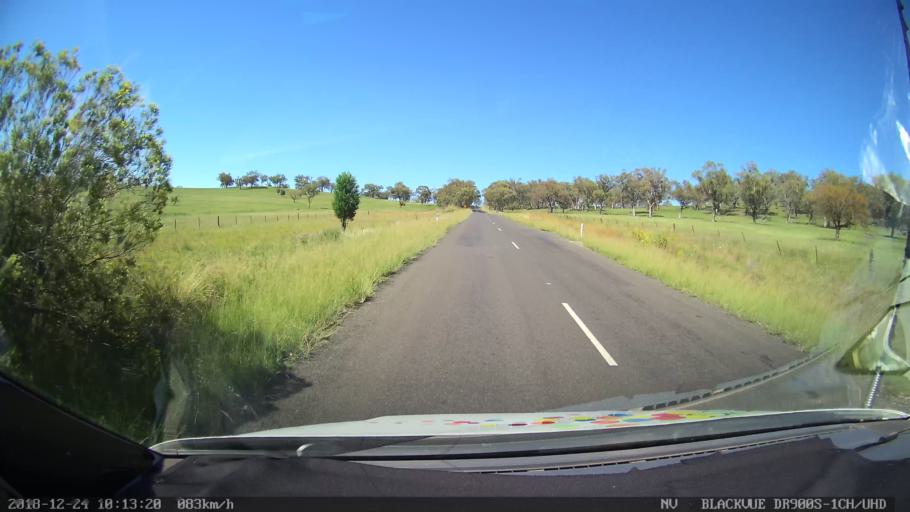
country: AU
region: New South Wales
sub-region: Liverpool Plains
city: Quirindi
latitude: -31.6888
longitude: 150.6404
